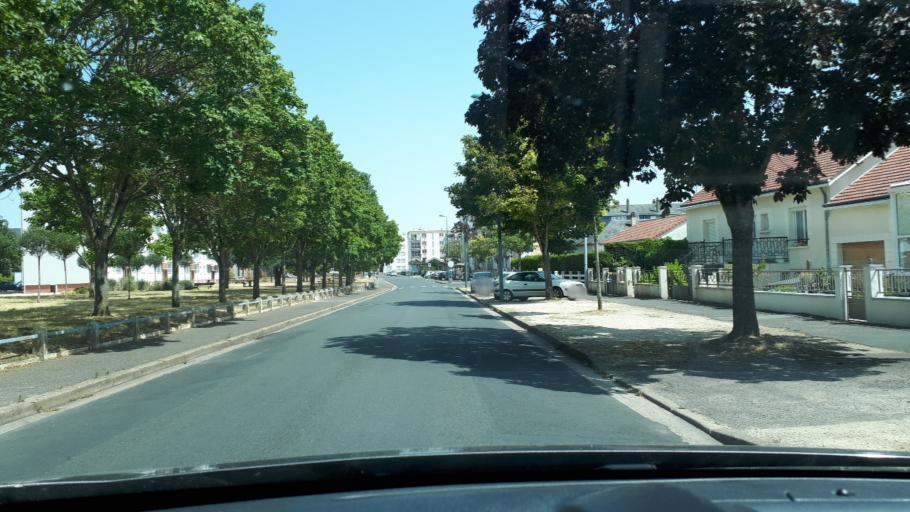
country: FR
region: Centre
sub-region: Departement du Loir-et-Cher
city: Vendome
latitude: 47.8071
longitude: 1.0633
